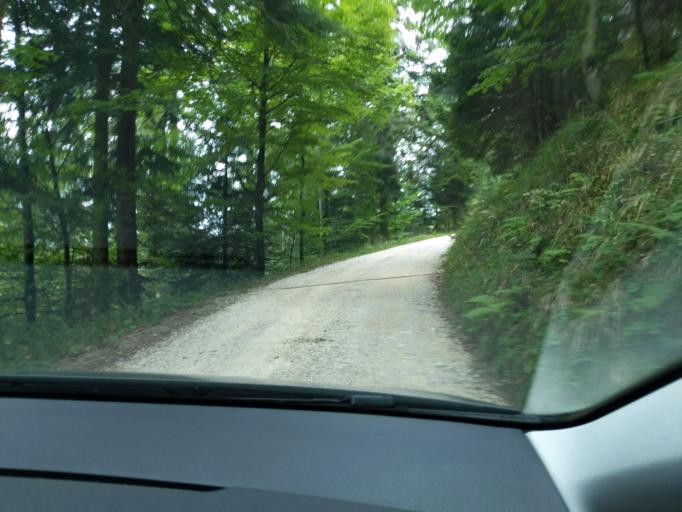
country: CH
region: Bern
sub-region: Oberaargau
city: Wyssachen
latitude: 47.0337
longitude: 7.8300
